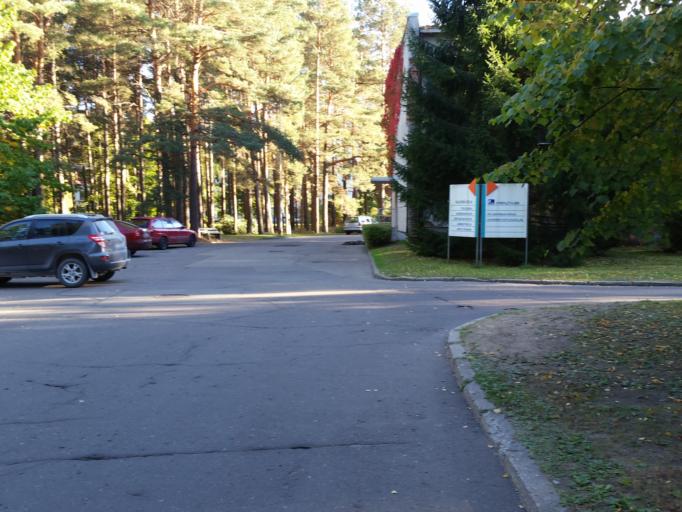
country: LV
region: Riga
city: Jaunciems
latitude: 56.9758
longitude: 24.1977
